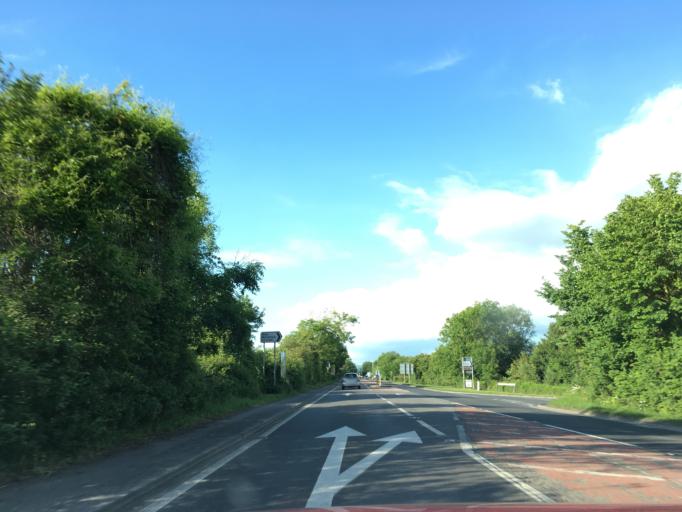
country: GB
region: England
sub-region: Somerset
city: Highbridge
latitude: 51.2343
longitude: -2.9558
